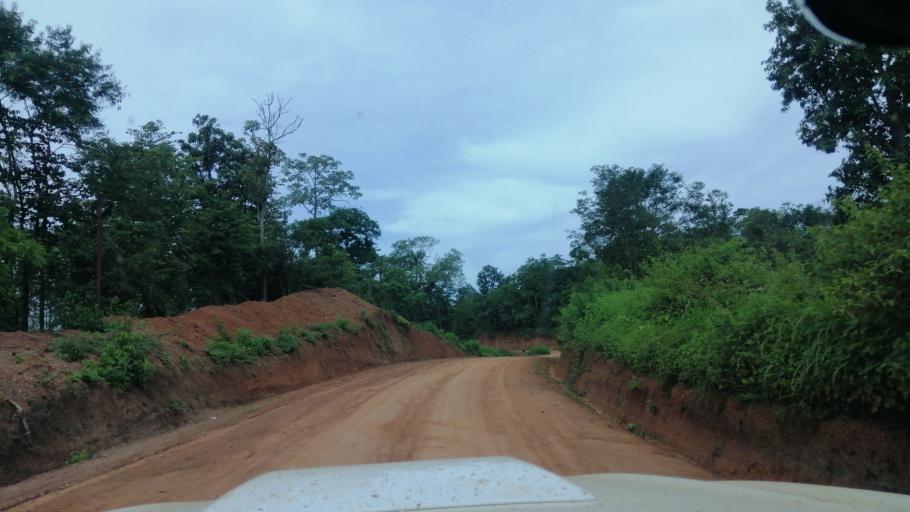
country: TH
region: Loei
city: Na Haeo
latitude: 17.5819
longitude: 101.1487
